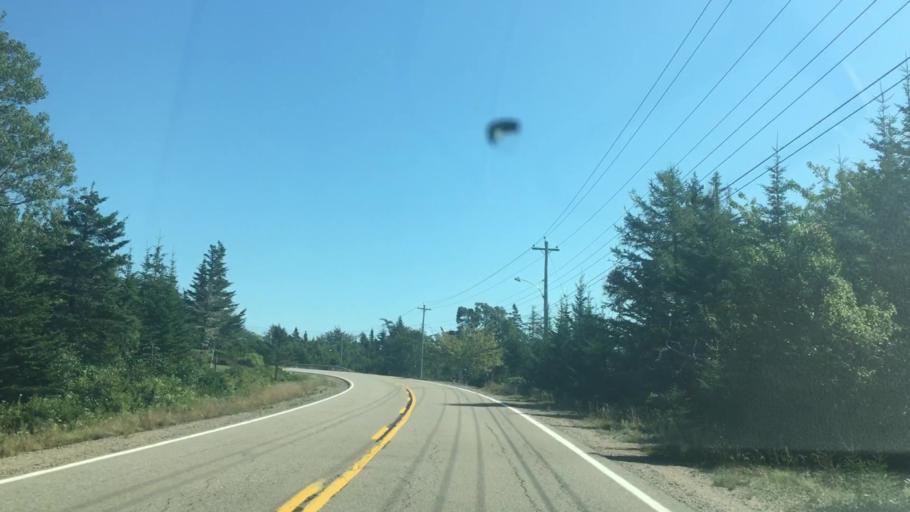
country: CA
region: Nova Scotia
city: Antigonish
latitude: 45.0215
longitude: -62.0081
